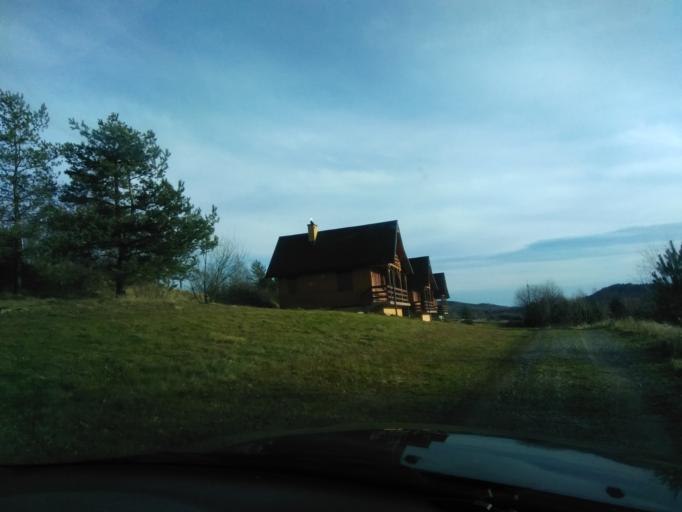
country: PL
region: Subcarpathian Voivodeship
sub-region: Powiat krosnienski
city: Korczyna
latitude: 49.7497
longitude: 21.7955
